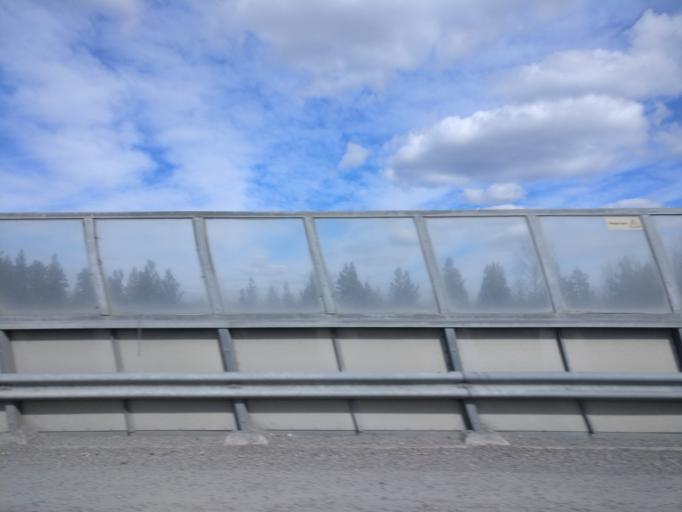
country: FI
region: Haeme
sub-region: Haemeenlinna
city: Parola
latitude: 61.0586
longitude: 24.3412
